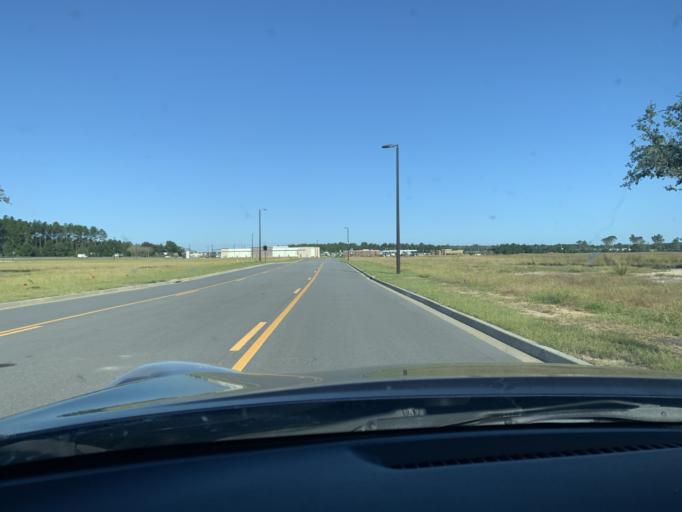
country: US
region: Georgia
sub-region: Chatham County
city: Pooler
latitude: 32.0756
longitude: -81.2781
